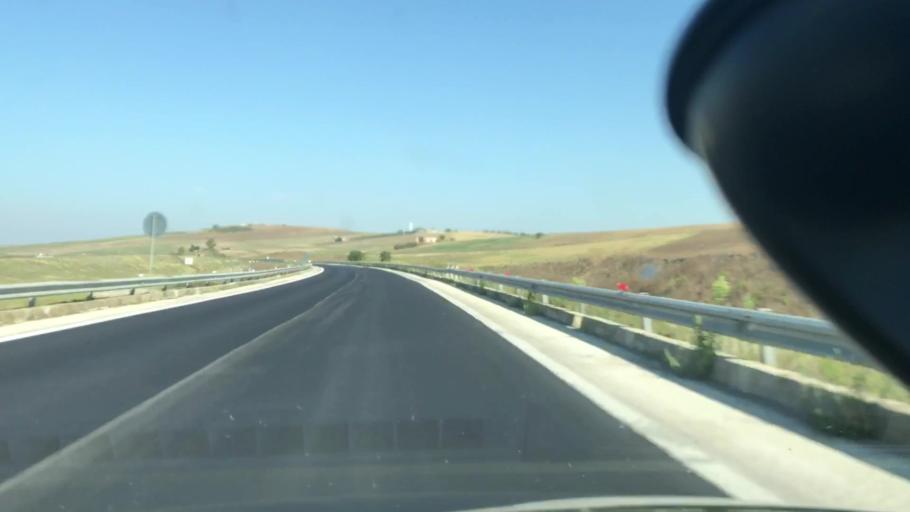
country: IT
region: Apulia
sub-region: Provincia di Barletta - Andria - Trani
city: Spinazzola
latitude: 40.9168
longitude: 16.1017
